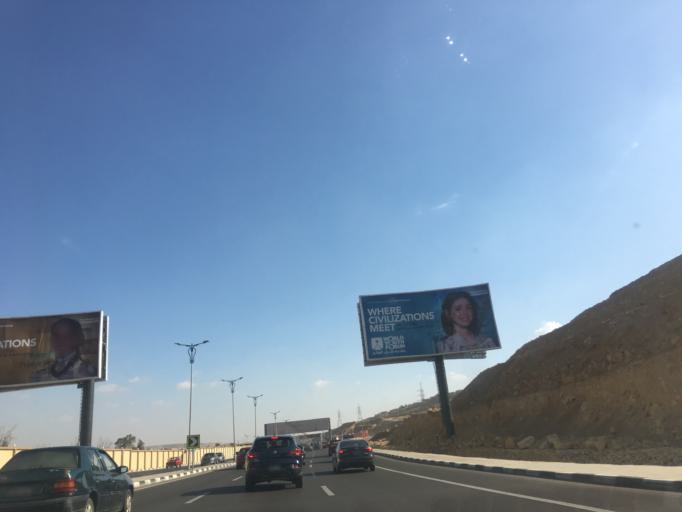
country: EG
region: Muhafazat al Qahirah
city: Cairo
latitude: 30.0255
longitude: 31.3223
